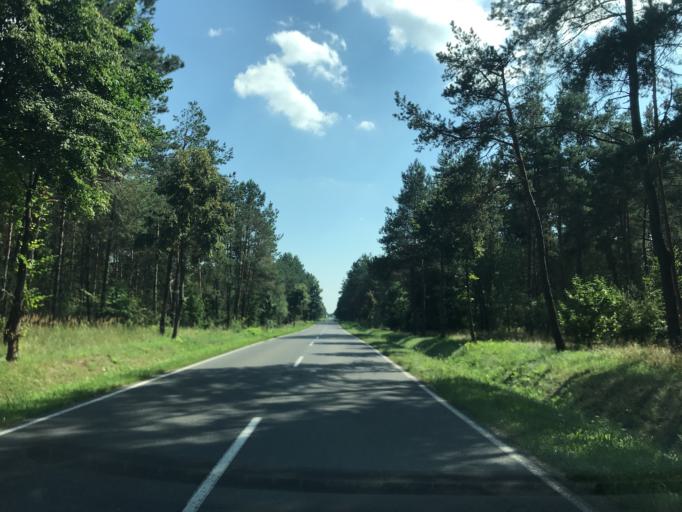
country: PL
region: Masovian Voivodeship
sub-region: Powiat zurominski
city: Lubowidz
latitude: 53.1887
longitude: 19.8480
